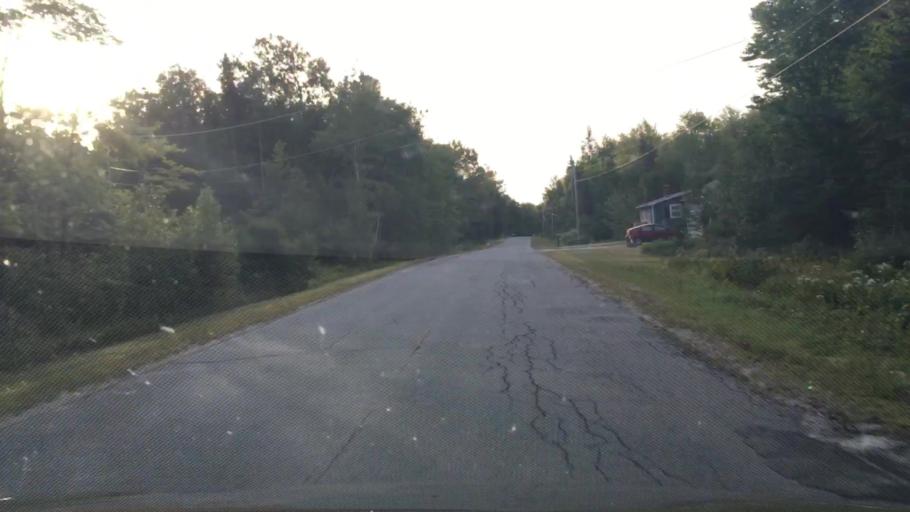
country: US
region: Maine
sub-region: Waldo County
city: Stockton Springs
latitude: 44.4939
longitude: -68.8732
